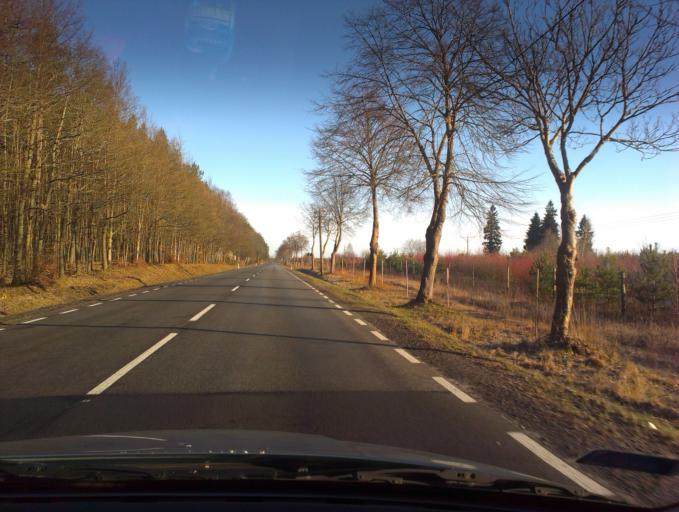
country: PL
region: West Pomeranian Voivodeship
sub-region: Powiat szczecinecki
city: Szczecinek
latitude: 53.8272
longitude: 16.6375
